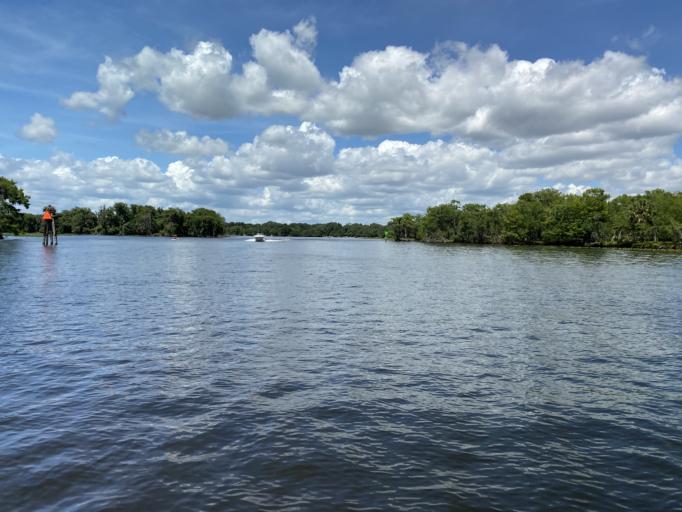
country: US
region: Florida
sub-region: Volusia County
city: DeBary
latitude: 28.8527
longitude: -81.3562
